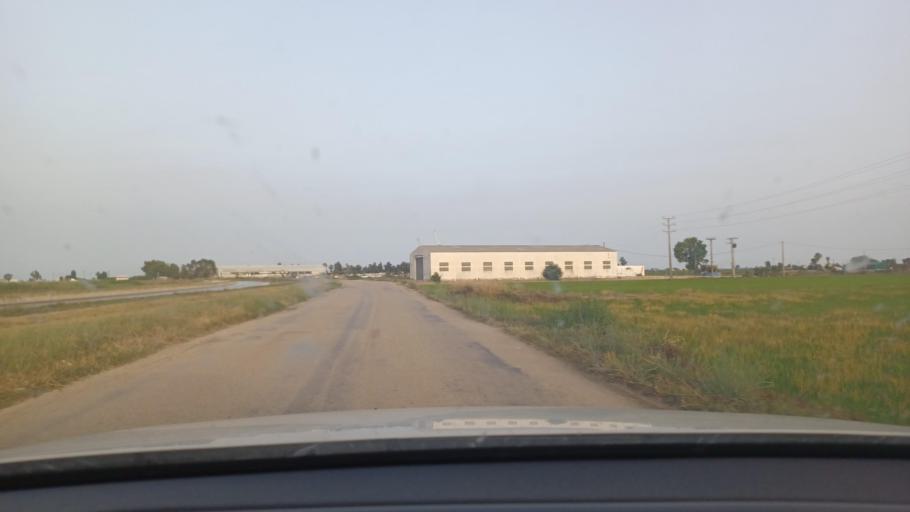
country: ES
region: Catalonia
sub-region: Provincia de Tarragona
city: Amposta
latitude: 40.7025
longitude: 0.5973
